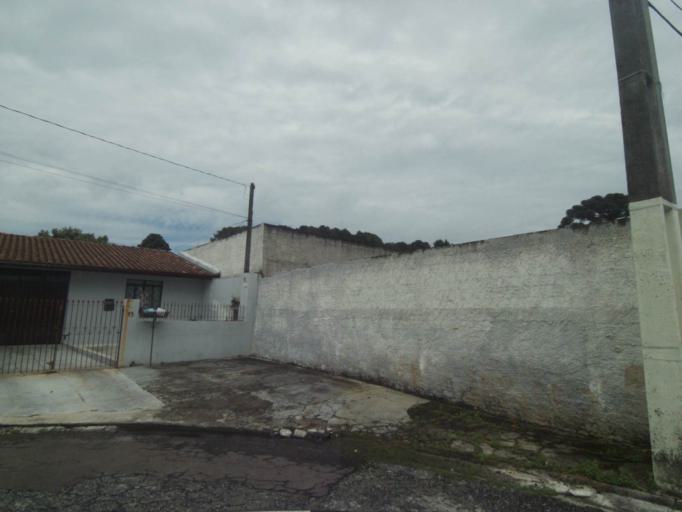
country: BR
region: Parana
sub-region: Pinhais
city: Pinhais
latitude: -25.4736
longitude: -49.2017
